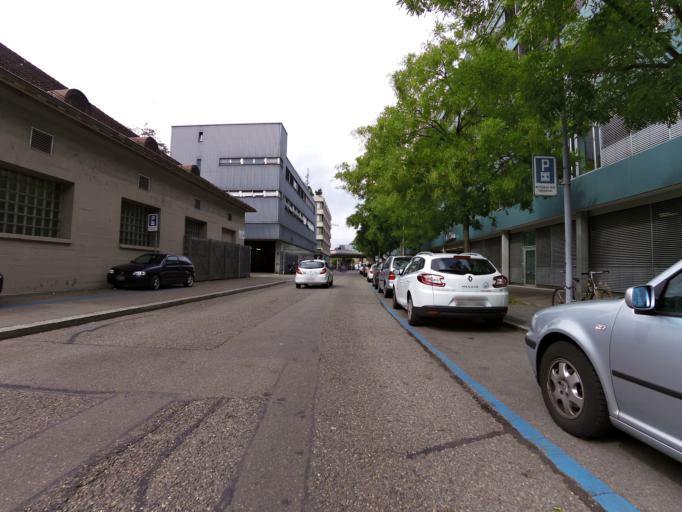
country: CH
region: Zurich
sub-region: Bezirk Zuerich
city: Zuerich (Kreis 5)
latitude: 47.3875
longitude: 8.5217
